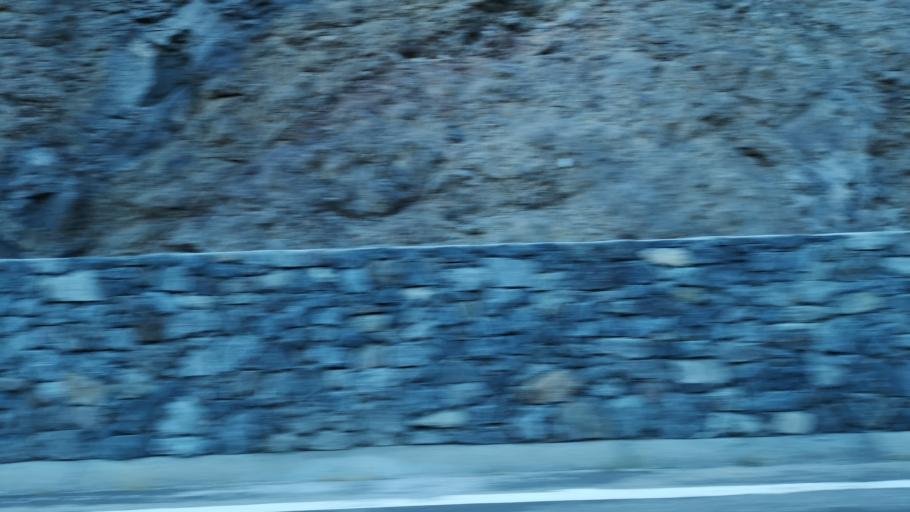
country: ES
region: Canary Islands
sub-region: Provincia de Santa Cruz de Tenerife
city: Alajero
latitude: 28.0332
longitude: -17.2061
